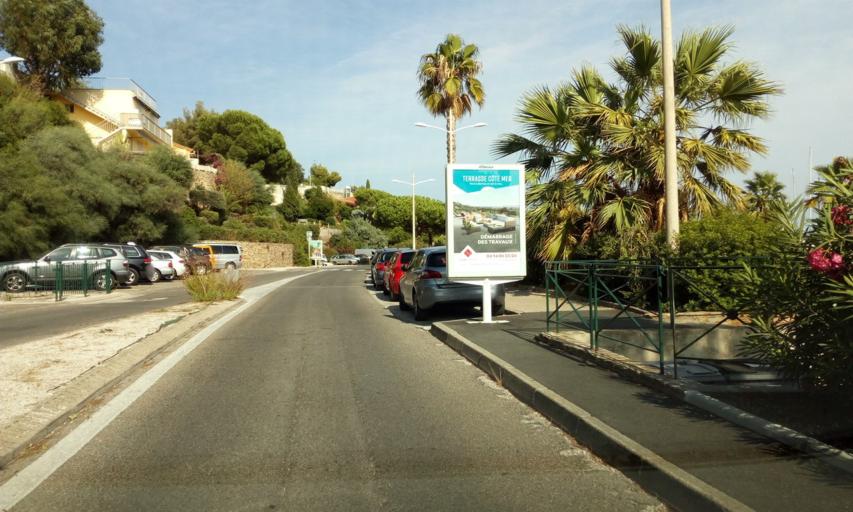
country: FR
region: Provence-Alpes-Cote d'Azur
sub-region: Departement du Var
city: Le Lavandou
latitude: 43.1375
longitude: 6.3749
